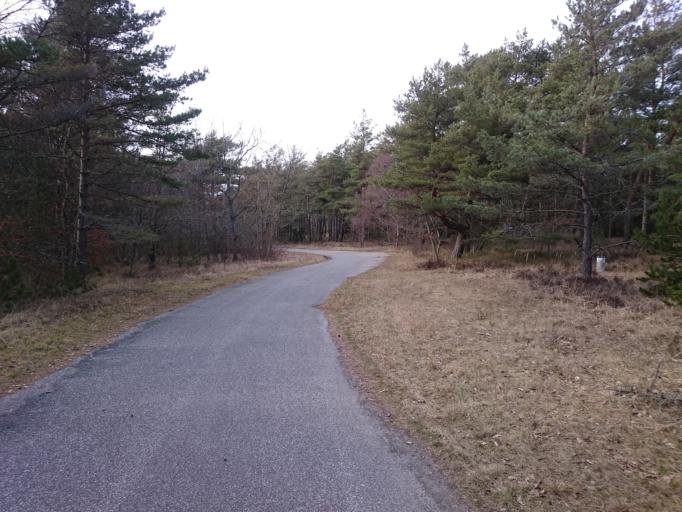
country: DK
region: North Denmark
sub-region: Frederikshavn Kommune
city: Skagen
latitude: 57.6995
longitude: 10.5189
